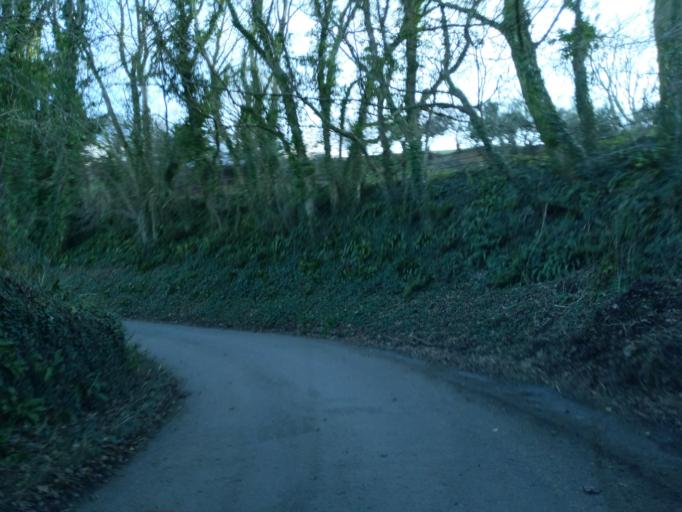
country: GB
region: England
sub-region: Cornwall
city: Pillaton
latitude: 50.3970
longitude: -4.3312
